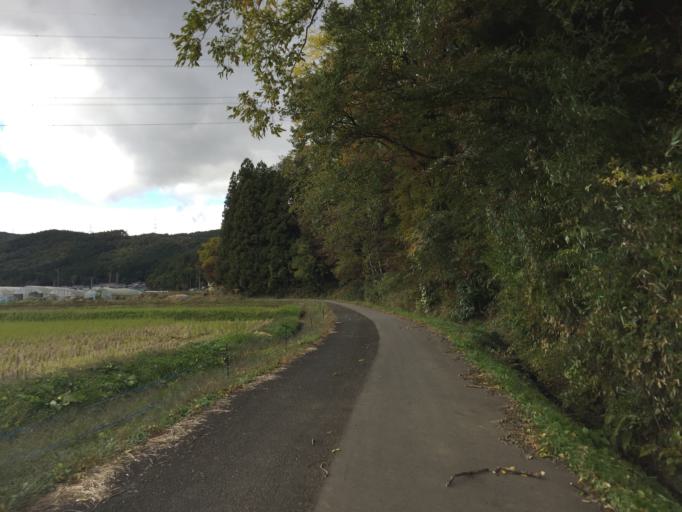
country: JP
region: Fukushima
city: Nihommatsu
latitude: 37.6696
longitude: 140.4172
